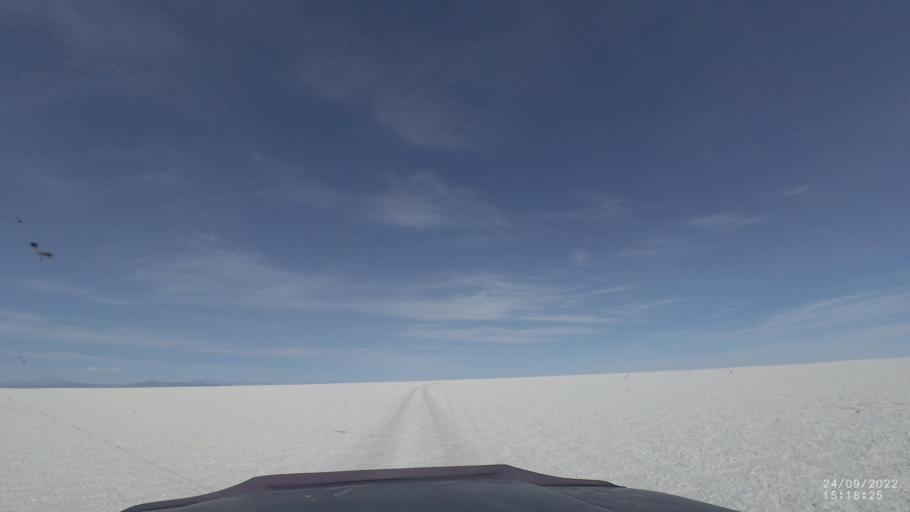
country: BO
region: Potosi
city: Colchani
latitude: -19.9964
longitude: -67.4191
